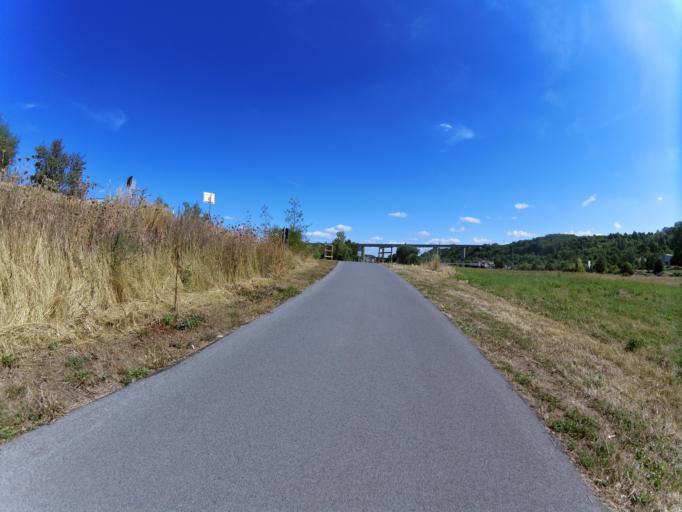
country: DE
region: Bavaria
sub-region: Regierungsbezirk Unterfranken
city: Frickenhausen
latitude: 49.6692
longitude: 10.1163
